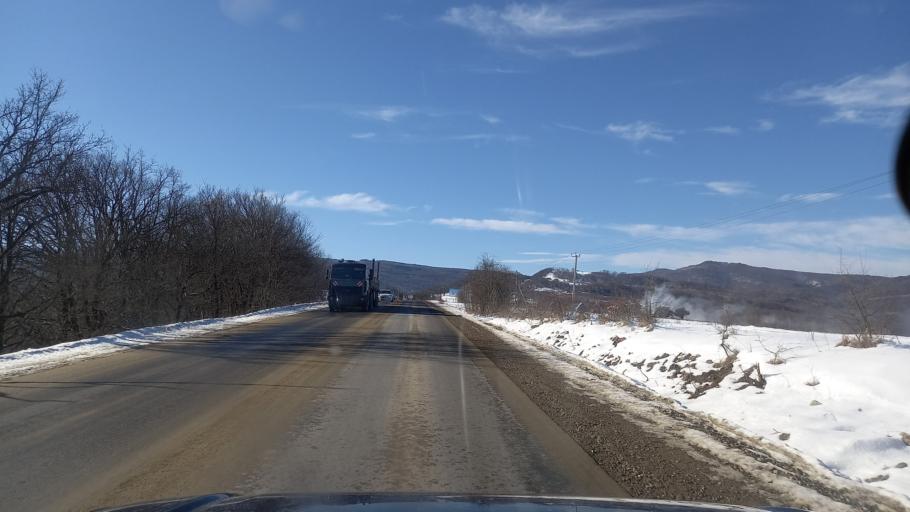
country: RU
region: Adygeya
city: Kamennomostskiy
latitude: 44.2361
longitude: 40.1530
